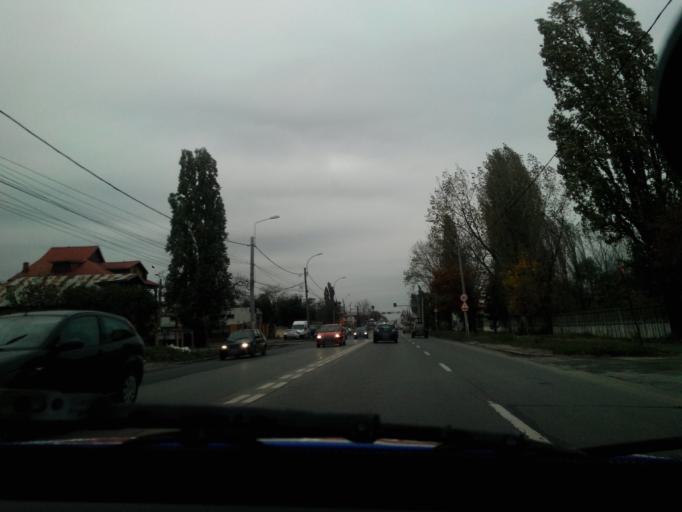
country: RO
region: Ilfov
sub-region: Comuna Magurele
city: Magurele
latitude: 44.3936
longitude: 26.0300
